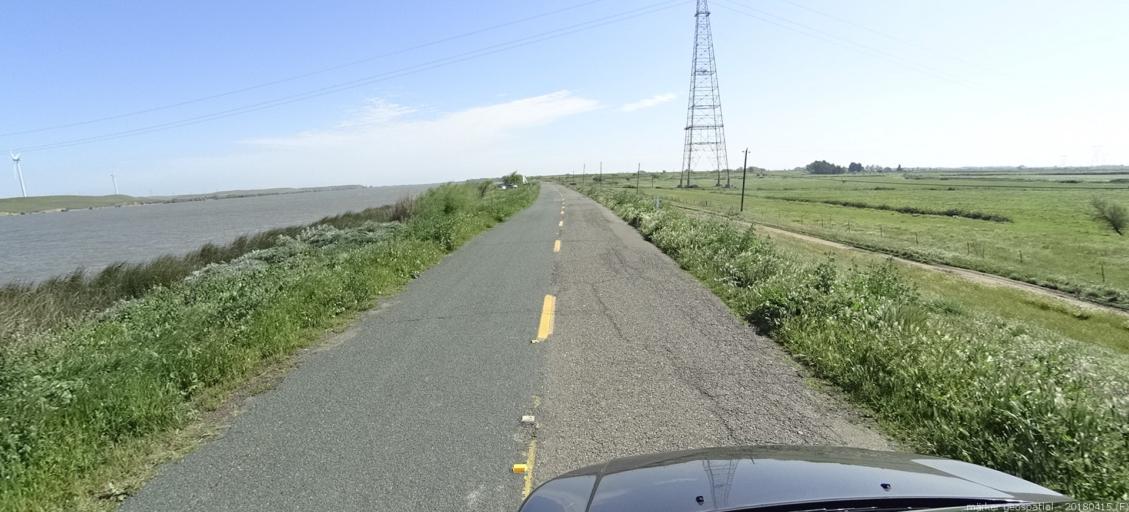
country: US
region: California
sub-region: Contra Costa County
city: Oakley
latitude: 38.0798
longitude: -121.7465
